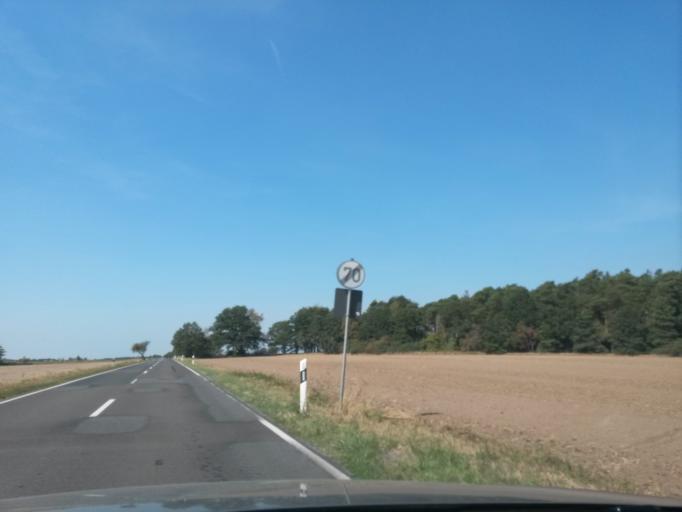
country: DE
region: Brandenburg
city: Wiesenburg
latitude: 52.1611
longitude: 12.4900
